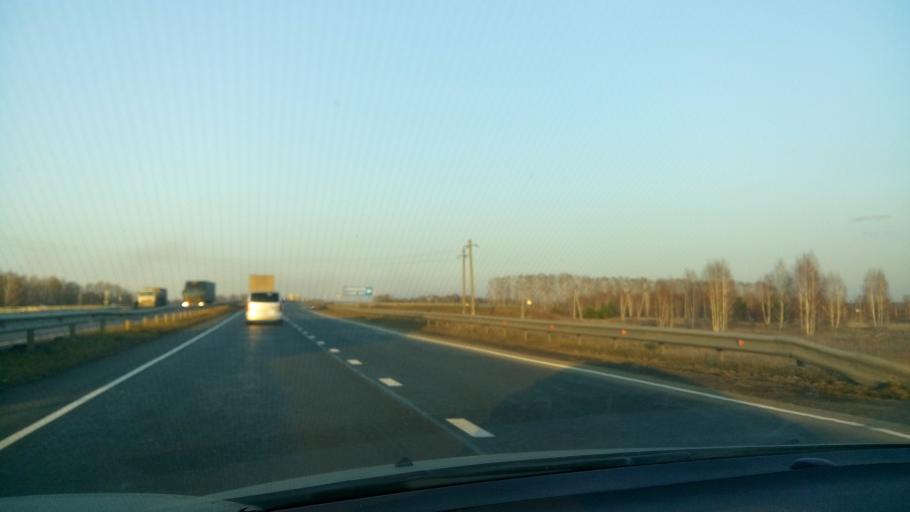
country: RU
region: Sverdlovsk
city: Yelanskiy
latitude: 56.8076
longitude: 62.5251
